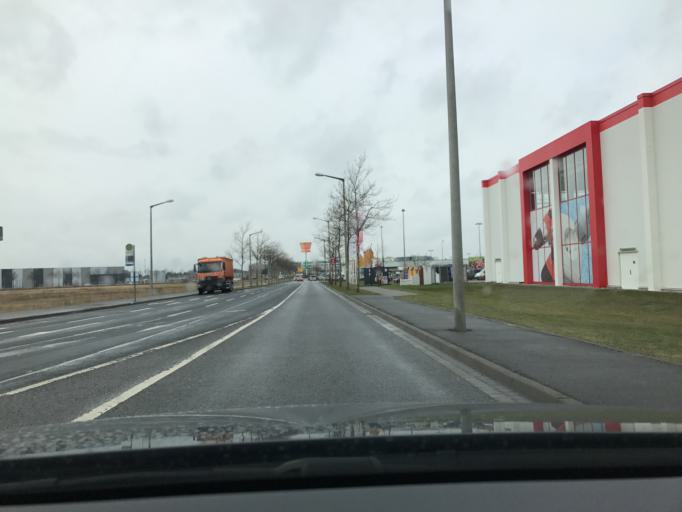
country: DE
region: Saxony
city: Rackwitz
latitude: 51.3990
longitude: 12.3982
